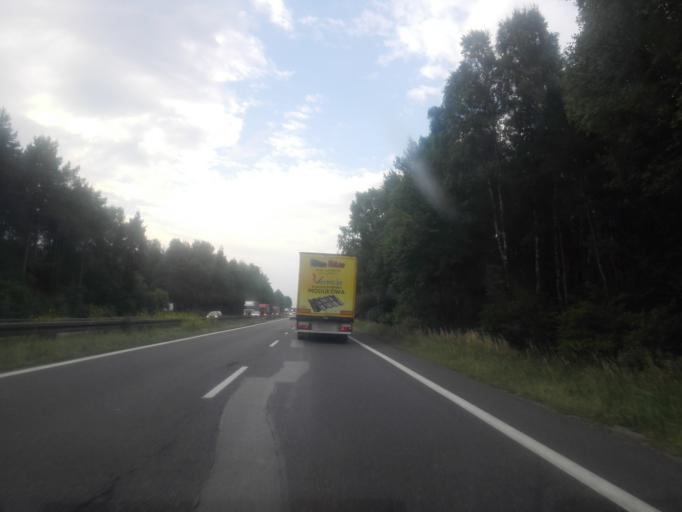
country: PL
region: Silesian Voivodeship
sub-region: Powiat bedzinski
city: Siewierz
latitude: 50.5194
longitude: 19.1937
